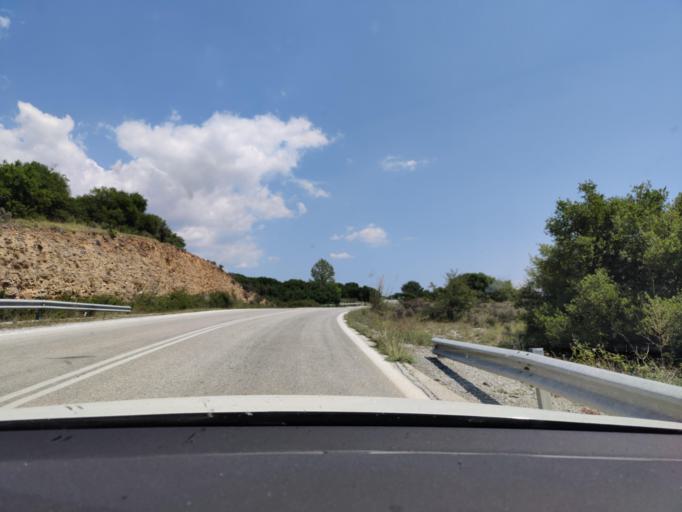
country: GR
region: East Macedonia and Thrace
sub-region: Nomos Kavalas
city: Paralia Ofryniou
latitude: 40.8074
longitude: 23.9777
